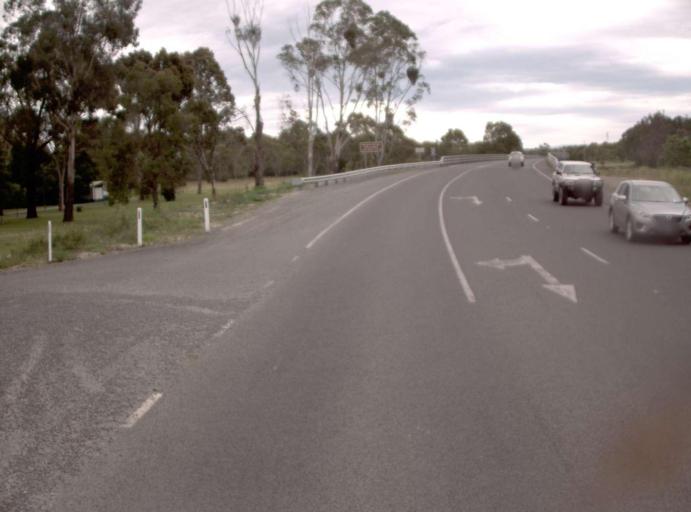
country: AU
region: Victoria
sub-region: Wellington
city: Sale
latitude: -38.1289
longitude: 147.0706
